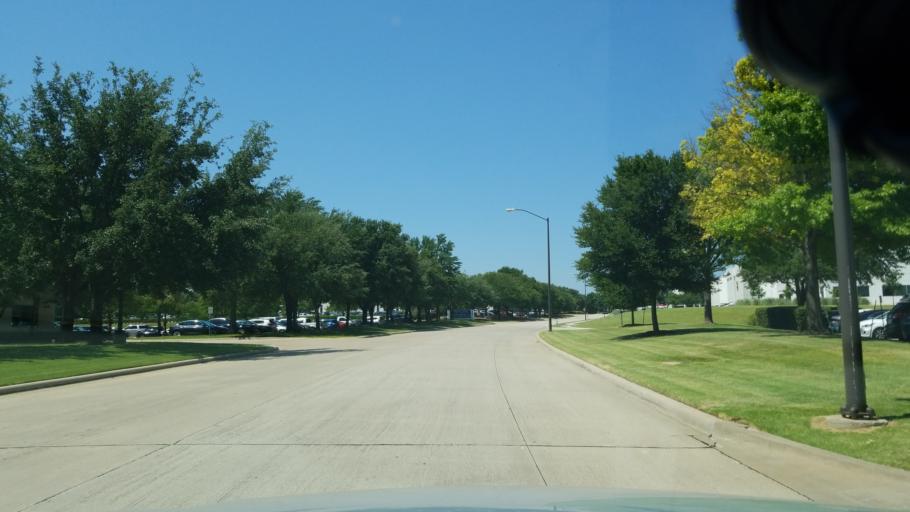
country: US
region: Texas
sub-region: Tarrant County
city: Euless
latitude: 32.8322
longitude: -97.0378
